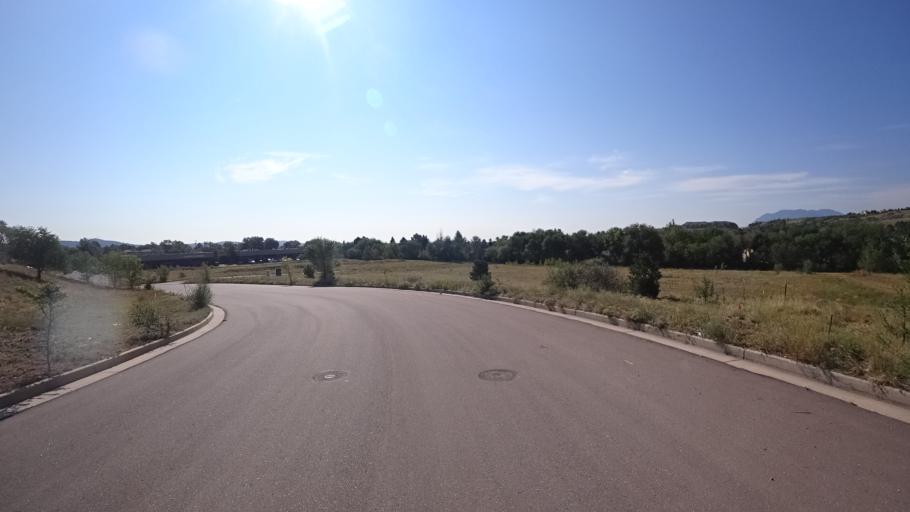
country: US
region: Colorado
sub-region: El Paso County
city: Colorado Springs
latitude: 38.8941
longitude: -104.8479
